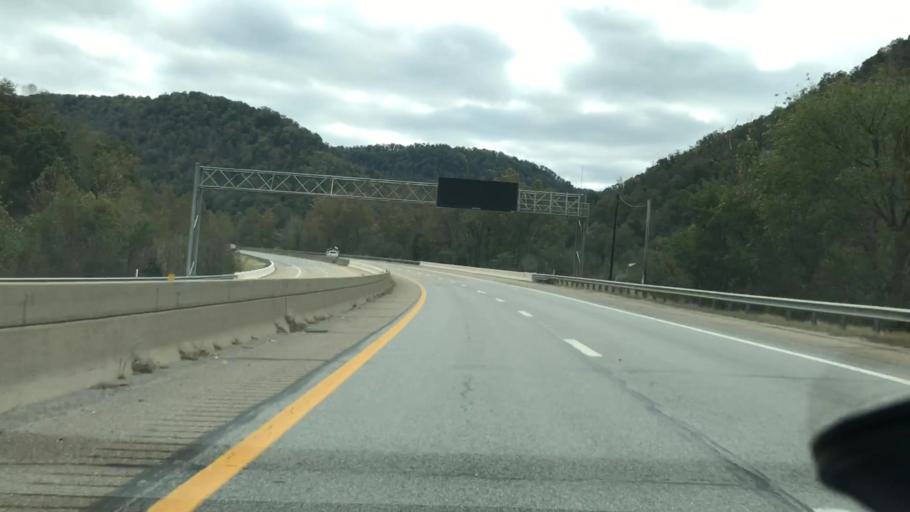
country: US
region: West Virginia
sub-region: Kanawha County
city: Chesapeake
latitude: 38.1816
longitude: -81.4661
